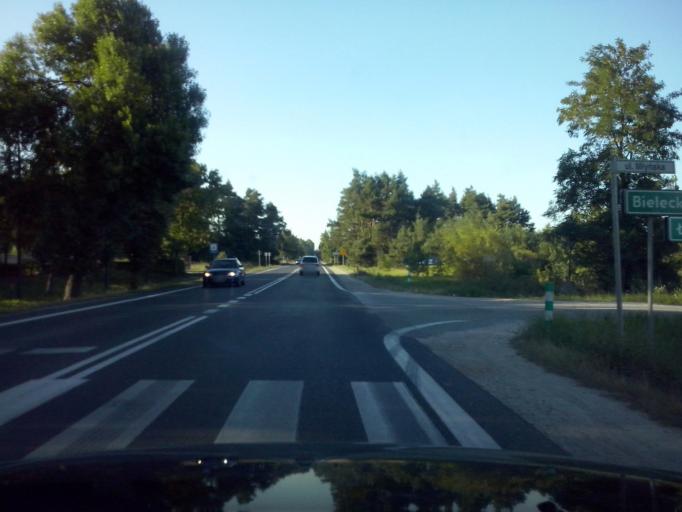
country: PL
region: Swietokrzyskie
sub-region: Powiat kielecki
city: Morawica
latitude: 50.7566
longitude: 20.6185
